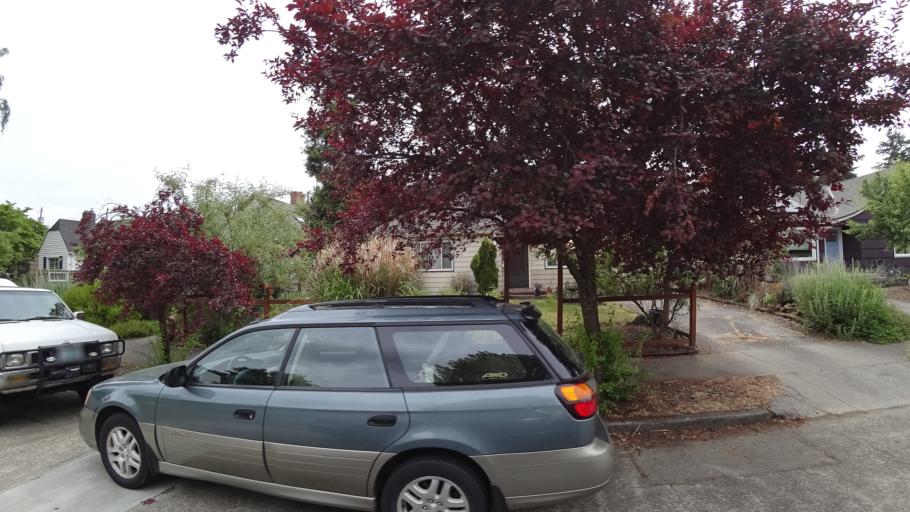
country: US
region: Oregon
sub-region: Multnomah County
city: Portland
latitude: 45.5693
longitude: -122.6759
